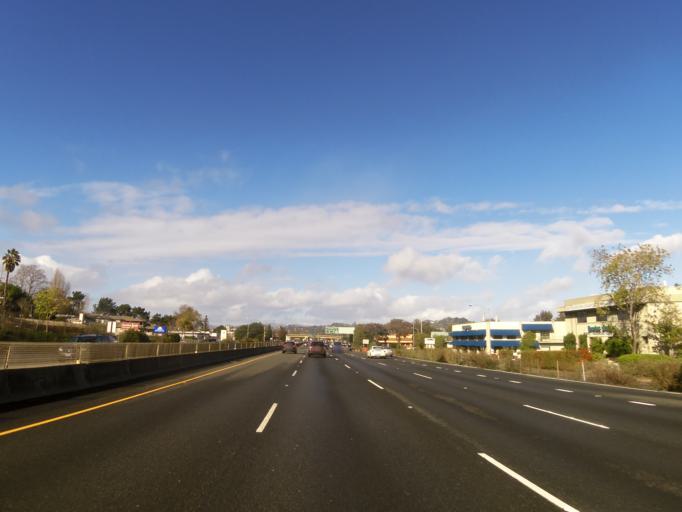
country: US
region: California
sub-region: Marin County
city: Corte Madera
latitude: 37.9217
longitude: -122.5123
